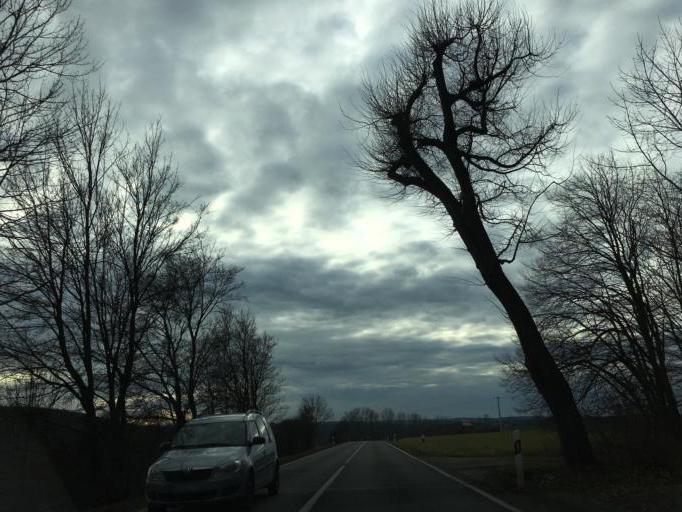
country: DE
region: Thuringia
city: Hetschburg
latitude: 50.9181
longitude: 11.2946
